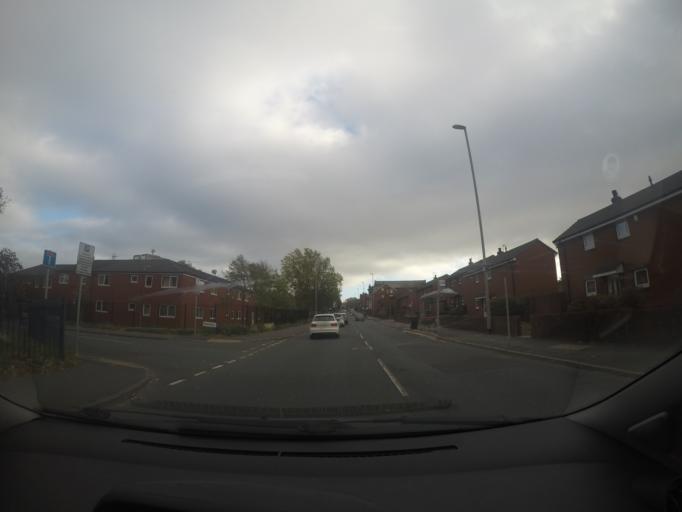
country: GB
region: England
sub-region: City and Borough of Leeds
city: Leeds
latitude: 53.7875
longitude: -1.5625
